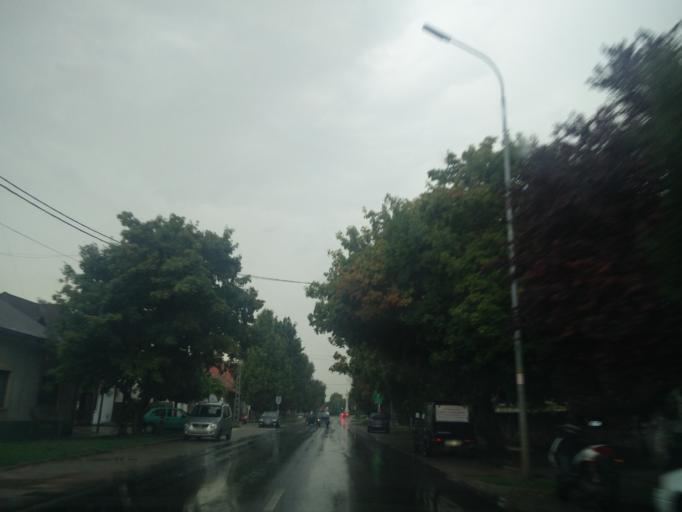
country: HU
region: Pest
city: Biatorbagy
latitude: 47.4641
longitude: 18.8094
